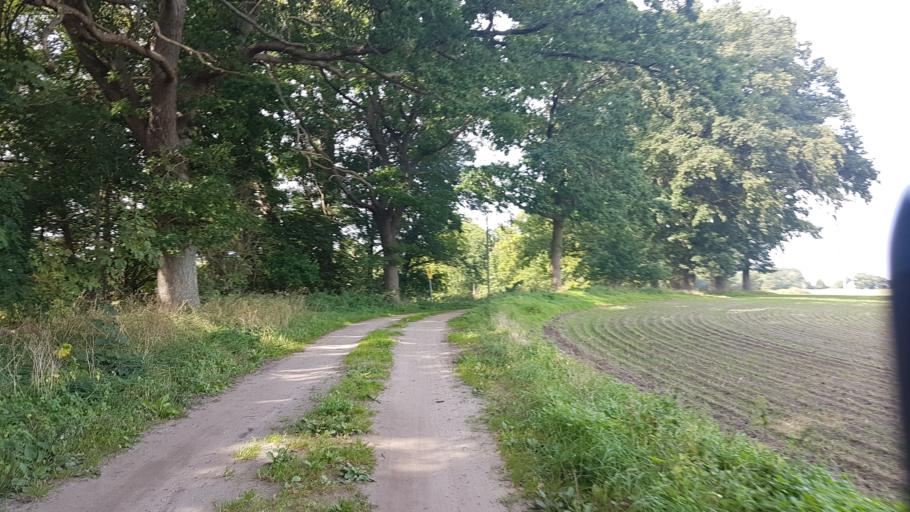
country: DE
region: Mecklenburg-Vorpommern
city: Samtens
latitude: 54.3902
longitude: 13.2641
